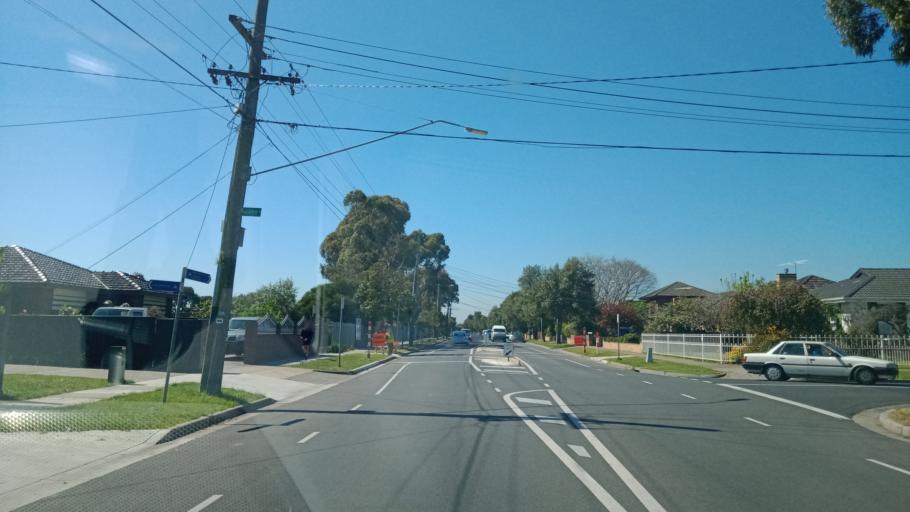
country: AU
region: Victoria
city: McKinnon
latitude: -37.9294
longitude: 145.0633
